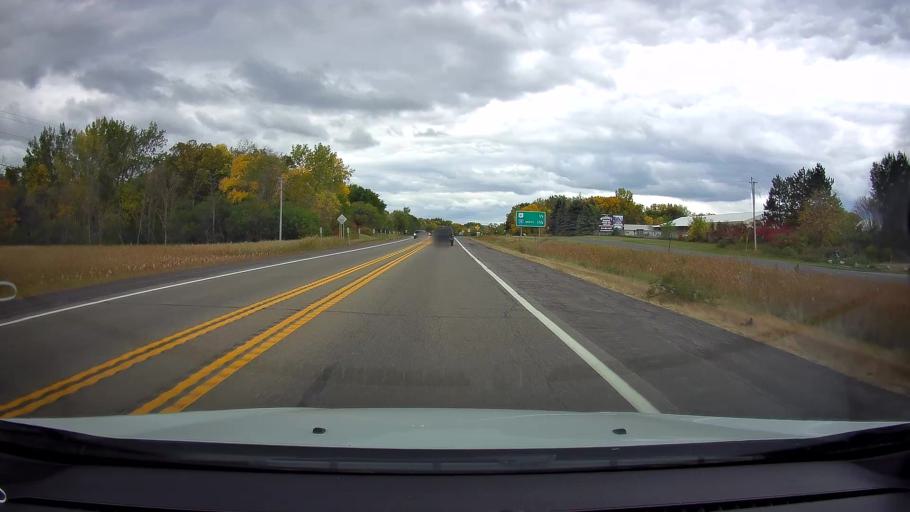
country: US
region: Minnesota
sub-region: Washington County
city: Forest Lake
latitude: 45.2963
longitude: -92.9742
